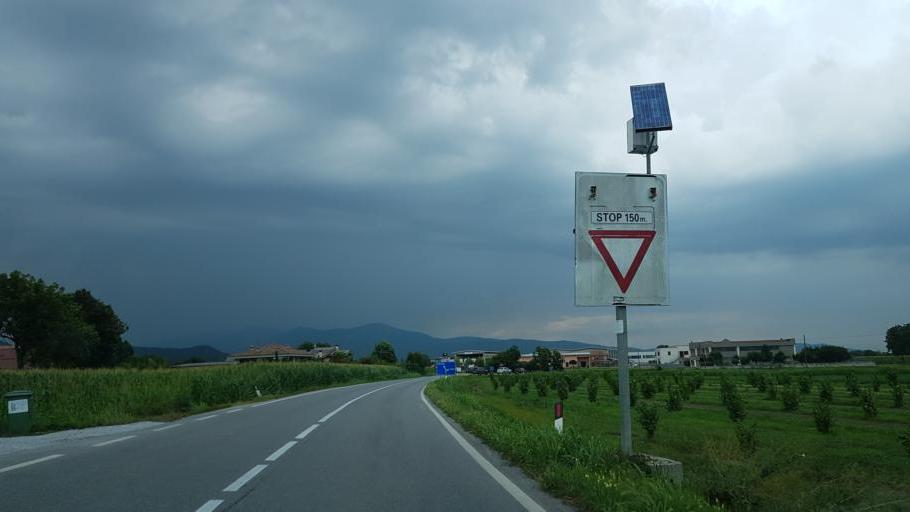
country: IT
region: Piedmont
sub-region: Provincia di Cuneo
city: Bernezzo
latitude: 44.3996
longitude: 7.4494
